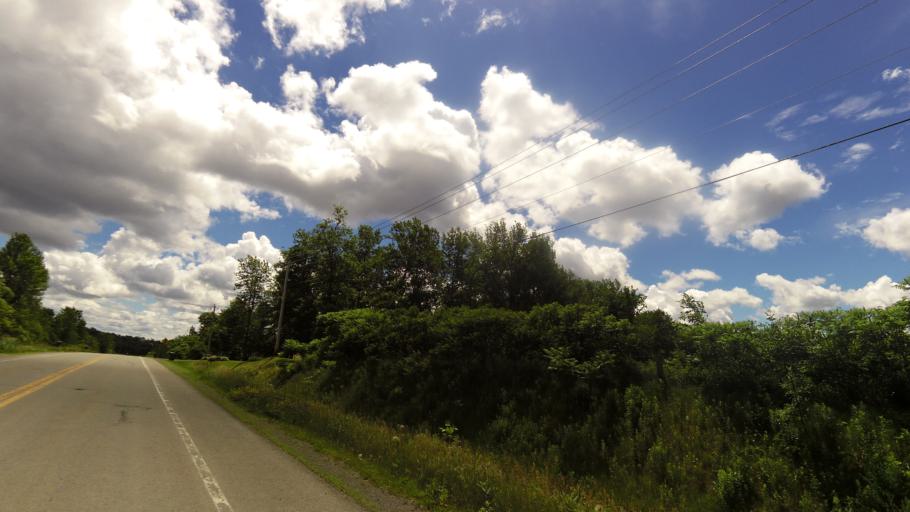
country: CA
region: Quebec
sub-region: Monteregie
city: Rigaud
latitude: 45.5314
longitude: -74.2999
